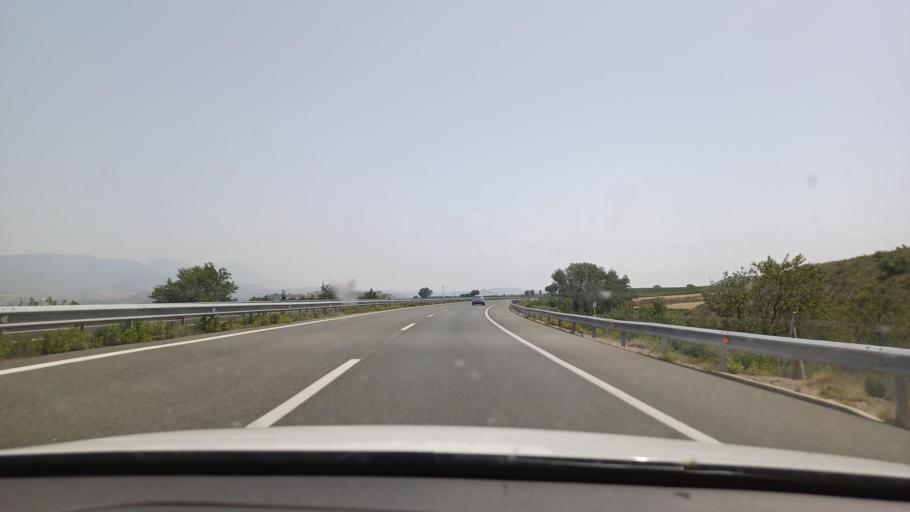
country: ES
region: La Rioja
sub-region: Provincia de La Rioja
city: Gimileo
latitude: 42.5394
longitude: -2.8121
